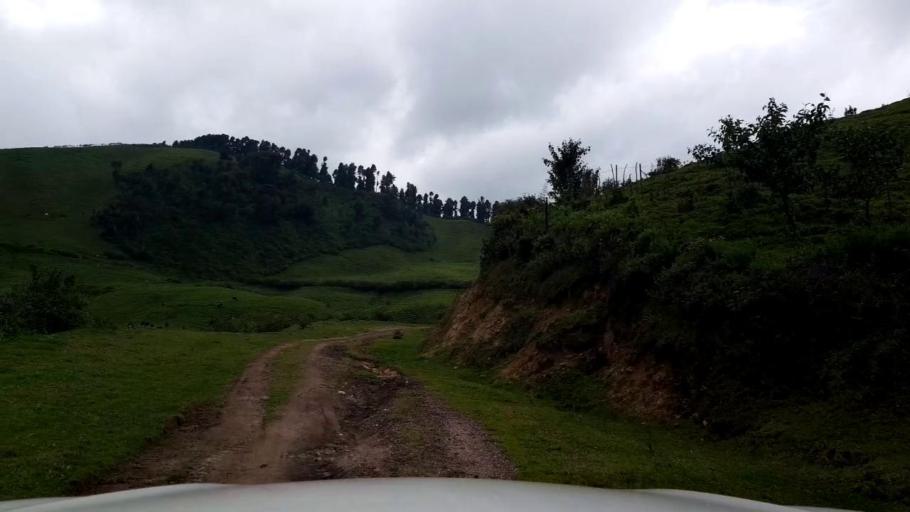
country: RW
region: Western Province
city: Gisenyi
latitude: -1.6915
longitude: 29.4252
